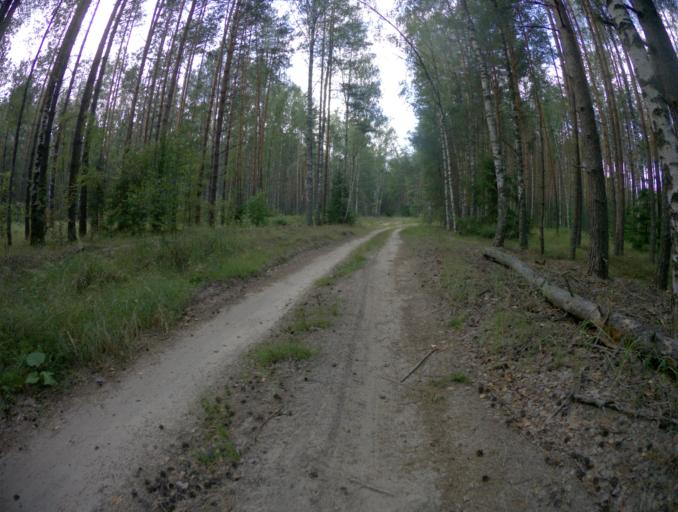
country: RU
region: Vladimir
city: Vorsha
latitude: 55.9639
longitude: 40.1884
